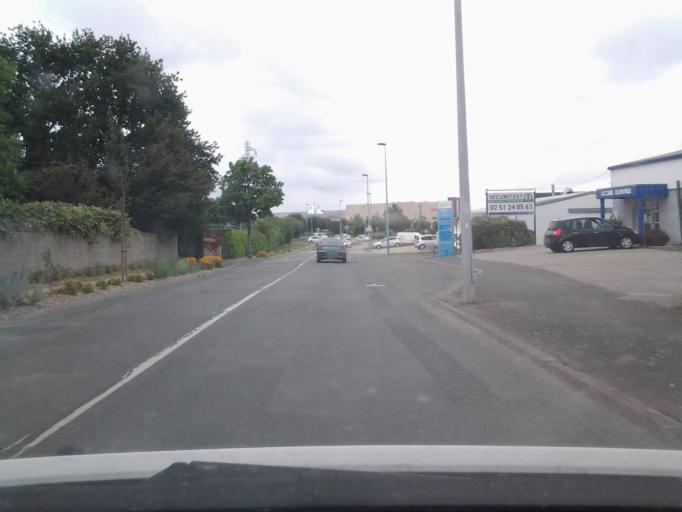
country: FR
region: Pays de la Loire
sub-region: Departement de la Vendee
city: La Roche-sur-Yon
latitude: 46.6510
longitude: -1.4319
